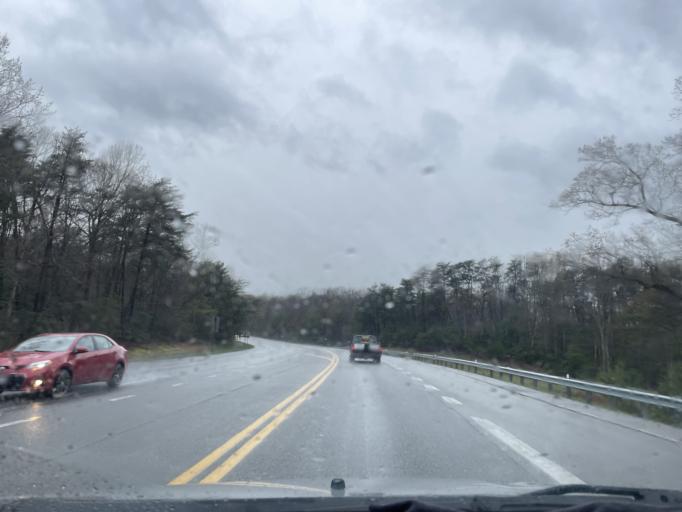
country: US
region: Maryland
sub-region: Saint Mary's County
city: California
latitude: 38.3111
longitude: -76.5119
